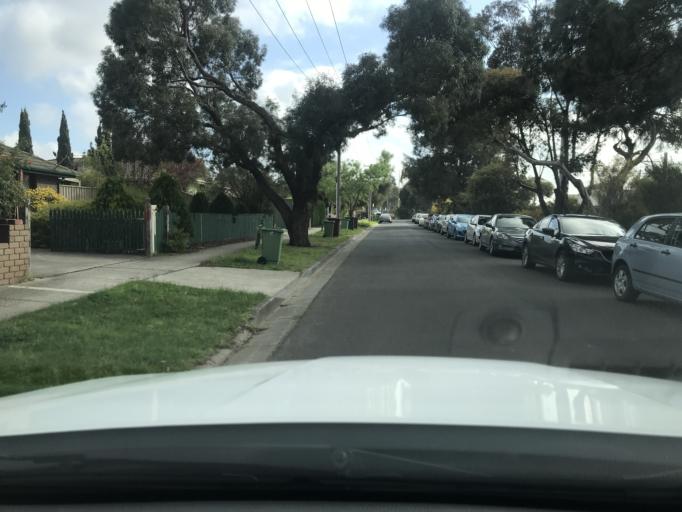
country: AU
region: Victoria
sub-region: Hume
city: Craigieburn
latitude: -37.6053
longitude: 144.9418
